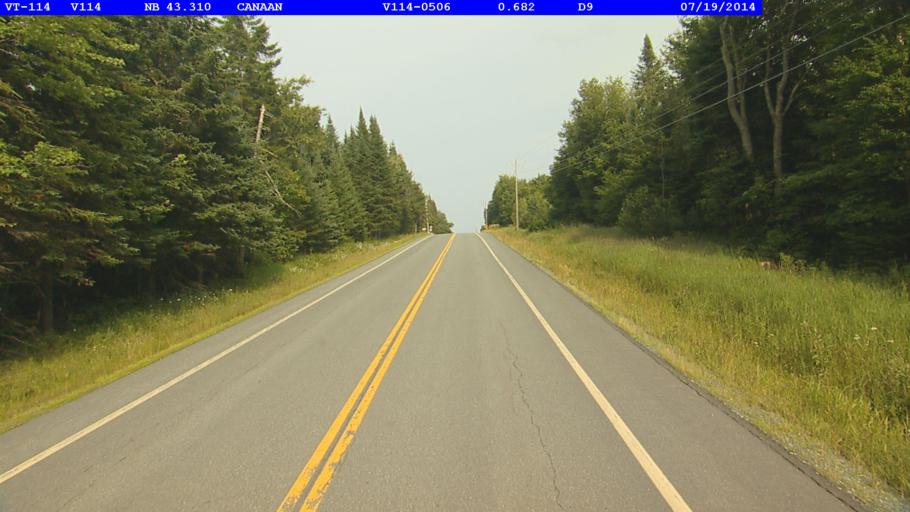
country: CA
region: Quebec
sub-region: Estrie
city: Coaticook
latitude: 45.0062
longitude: -71.6799
